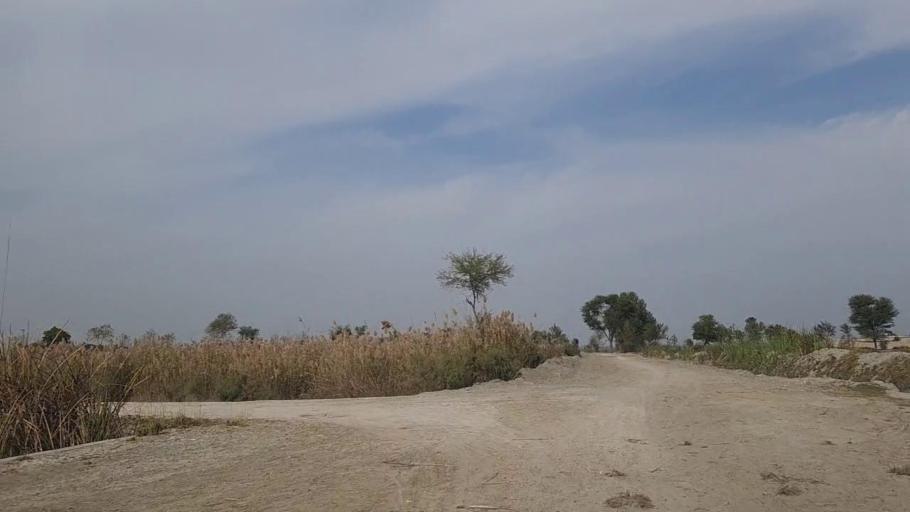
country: PK
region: Sindh
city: Daur
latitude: 26.4642
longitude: 68.4072
